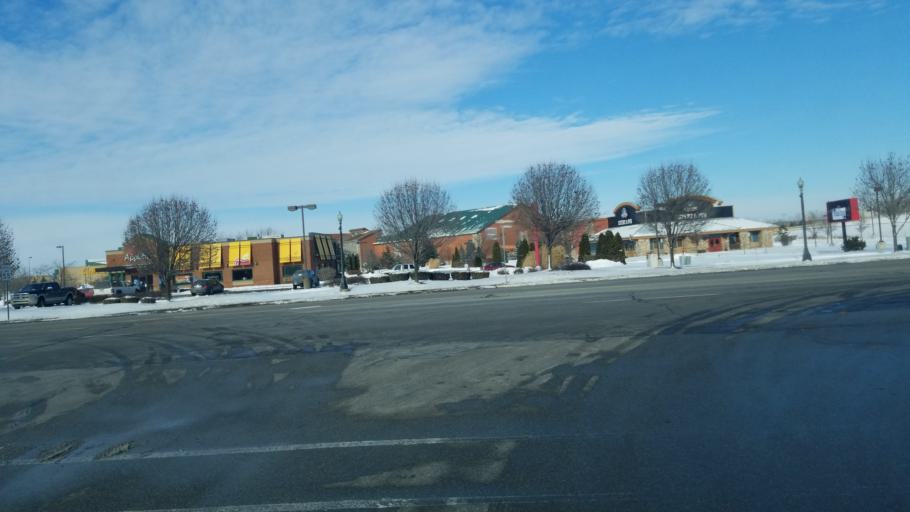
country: US
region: Michigan
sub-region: Monroe County
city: Dundee
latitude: 41.9595
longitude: -83.6745
